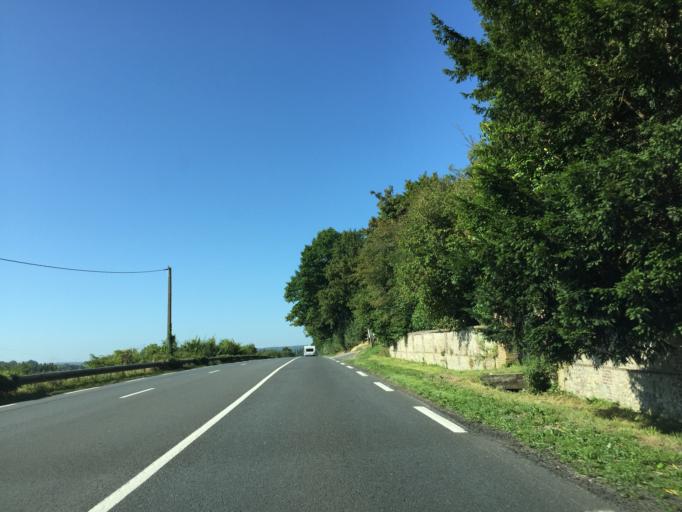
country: FR
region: Lower Normandy
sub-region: Departement du Calvados
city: Lisieux
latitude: 49.2460
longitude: 0.2212
